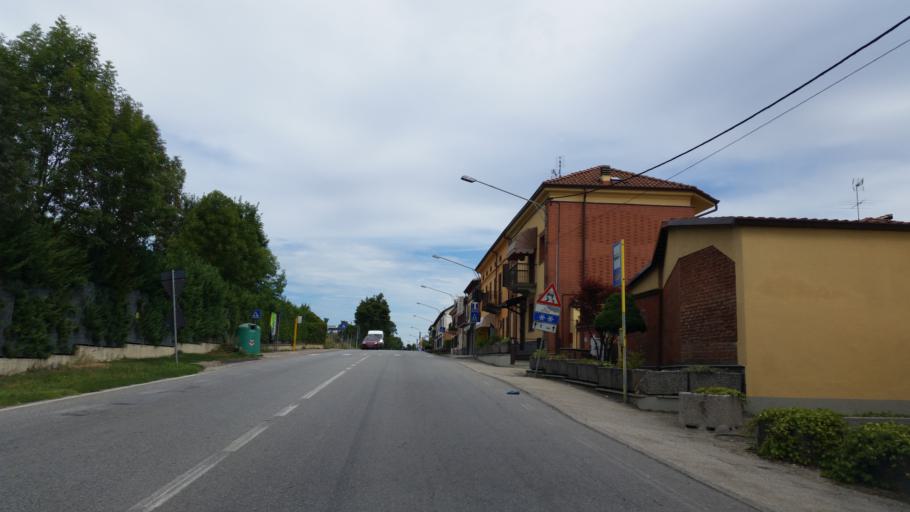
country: IT
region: Piedmont
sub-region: Provincia di Asti
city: Revigliasco d'Asti
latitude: 44.8994
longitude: 8.1471
